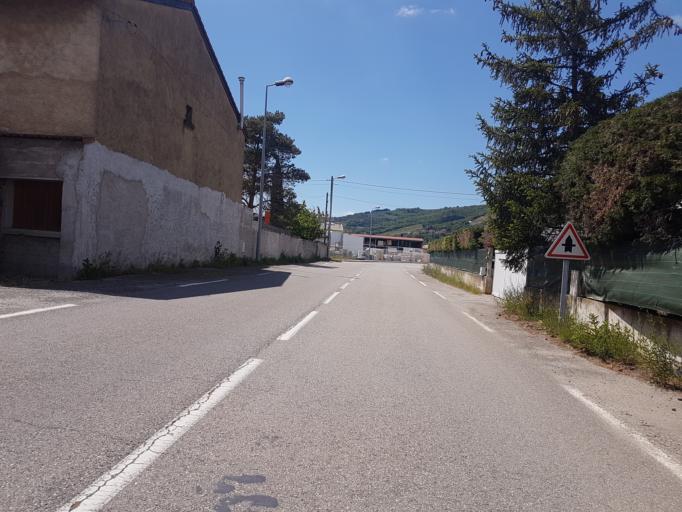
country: FR
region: Rhone-Alpes
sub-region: Departement de l'Ardeche
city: Saint-Jean-de-Muzols
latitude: 45.0767
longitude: 4.8187
